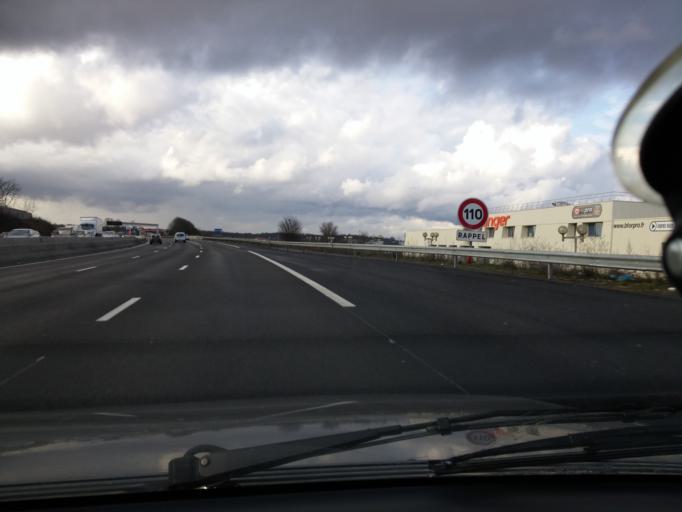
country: FR
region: Ile-de-France
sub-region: Departement de Seine-et-Marne
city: Emerainville
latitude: 48.8138
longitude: 2.6277
